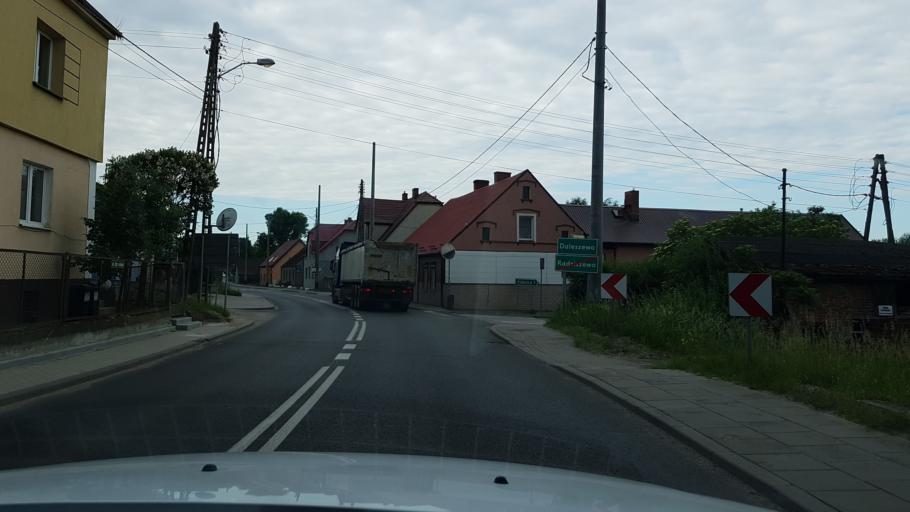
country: PL
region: West Pomeranian Voivodeship
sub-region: Powiat gryfinski
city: Gryfino
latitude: 53.3188
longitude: 14.5363
